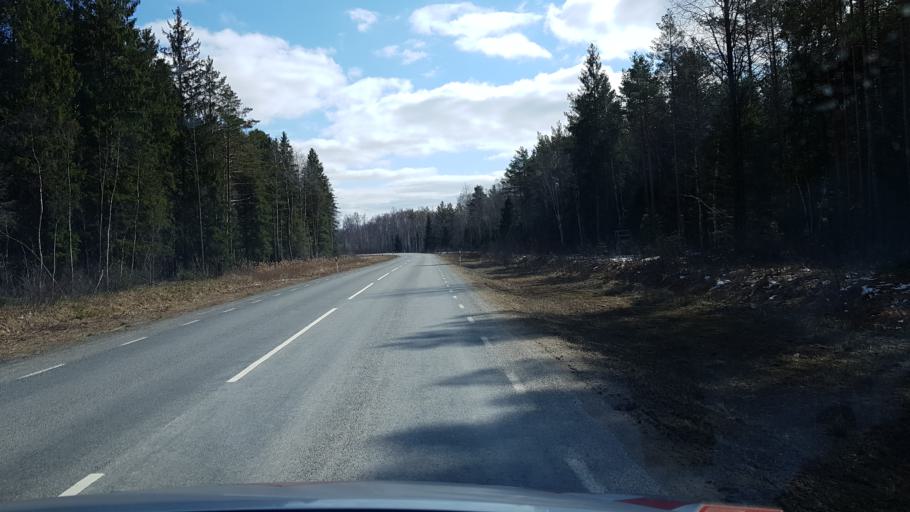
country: EE
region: Laeaene-Virumaa
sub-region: Tapa vald
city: Tapa
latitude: 59.2762
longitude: 25.9136
